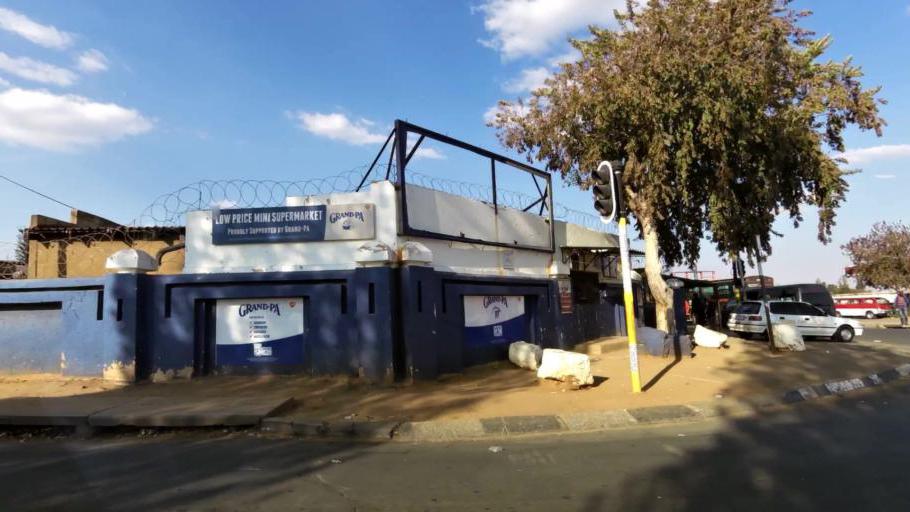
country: ZA
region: Gauteng
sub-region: City of Johannesburg Metropolitan Municipality
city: Roodepoort
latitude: -26.2142
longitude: 27.8761
